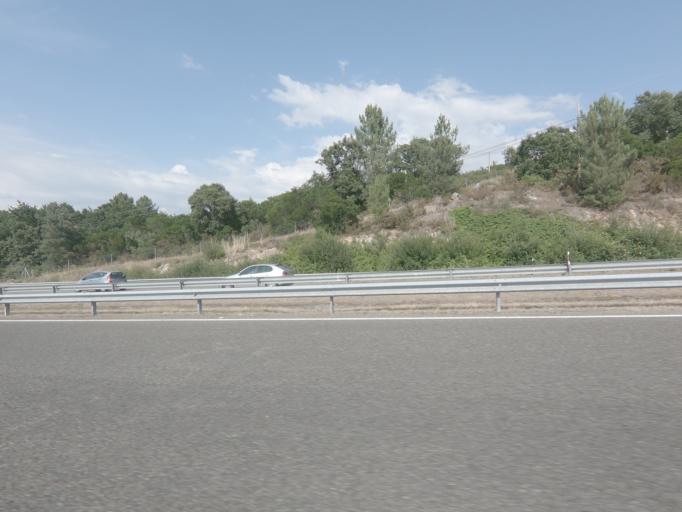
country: ES
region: Galicia
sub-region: Provincia de Ourense
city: Ourense
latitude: 42.2847
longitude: -7.8745
